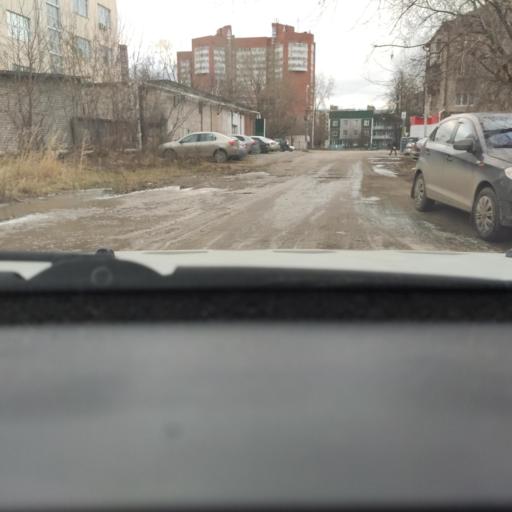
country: RU
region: Perm
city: Perm
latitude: 57.9673
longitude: 56.2365
